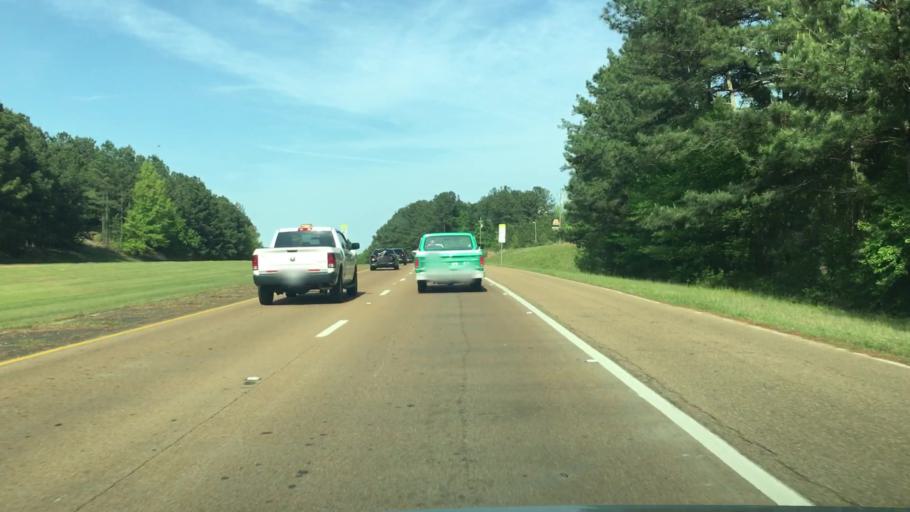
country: US
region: Mississippi
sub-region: Rankin County
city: Brandon
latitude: 32.3622
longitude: -89.9936
